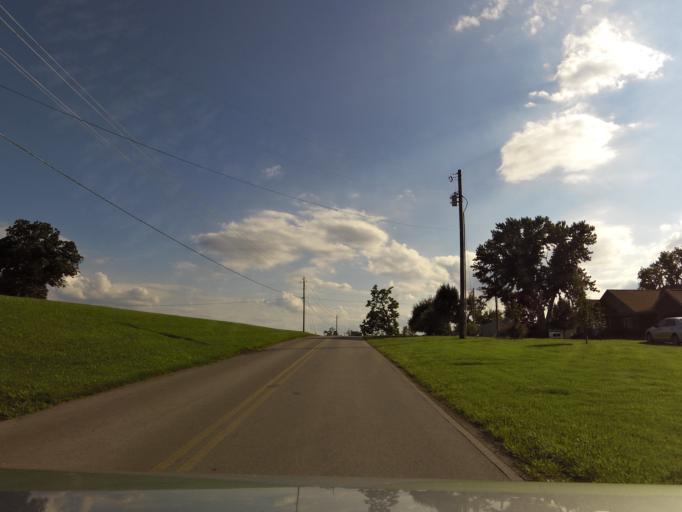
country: US
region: Tennessee
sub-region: Blount County
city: Maryville
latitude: 35.6809
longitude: -84.0505
